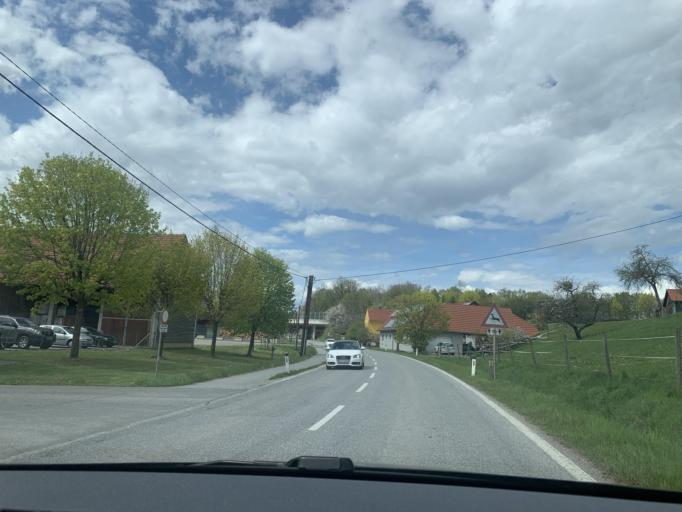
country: AT
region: Styria
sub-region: Politischer Bezirk Deutschlandsberg
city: Lannach
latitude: 46.9517
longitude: 15.3705
